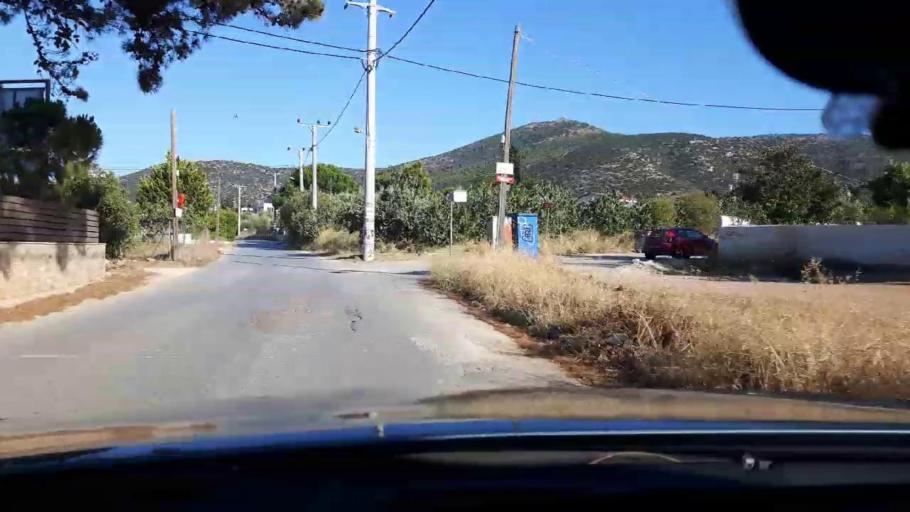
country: GR
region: Attica
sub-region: Nomarchia Anatolikis Attikis
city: Limin Mesoyaias
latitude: 37.8646
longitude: 24.0323
